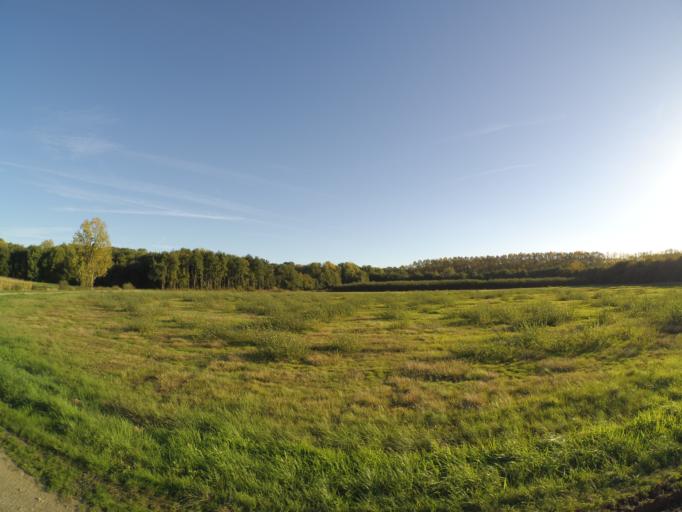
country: FR
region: Brittany
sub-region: Departement du Morbihan
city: Saint-Vincent-sur-Oust
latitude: 47.7240
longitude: -2.1697
